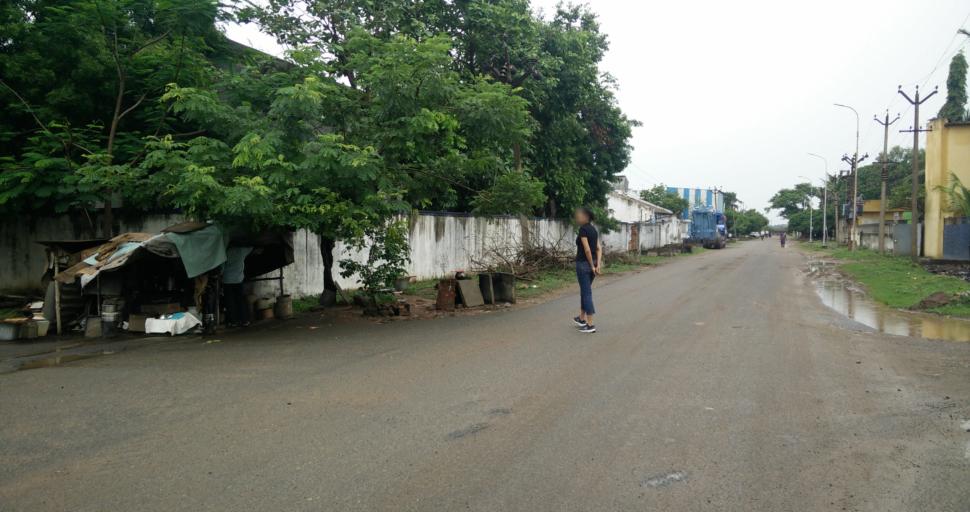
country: IN
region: Tamil Nadu
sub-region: Kancheepuram
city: Poonamalle
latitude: 13.0468
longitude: 80.0572
